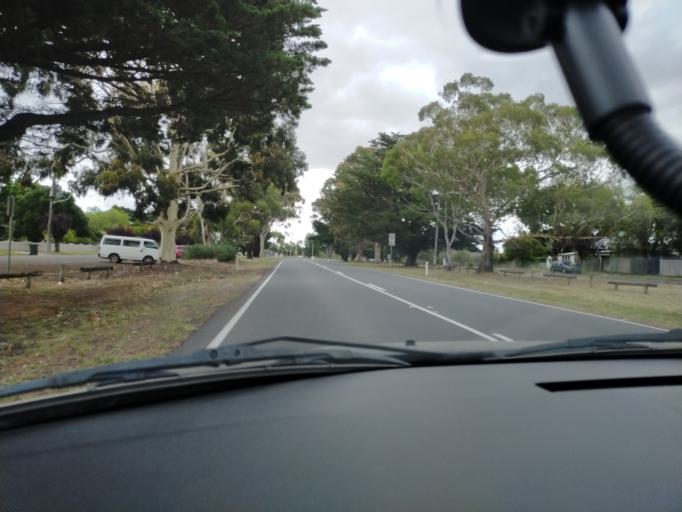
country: AU
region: Victoria
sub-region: Greater Geelong
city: Wandana Heights
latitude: -38.1017
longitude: 144.0527
